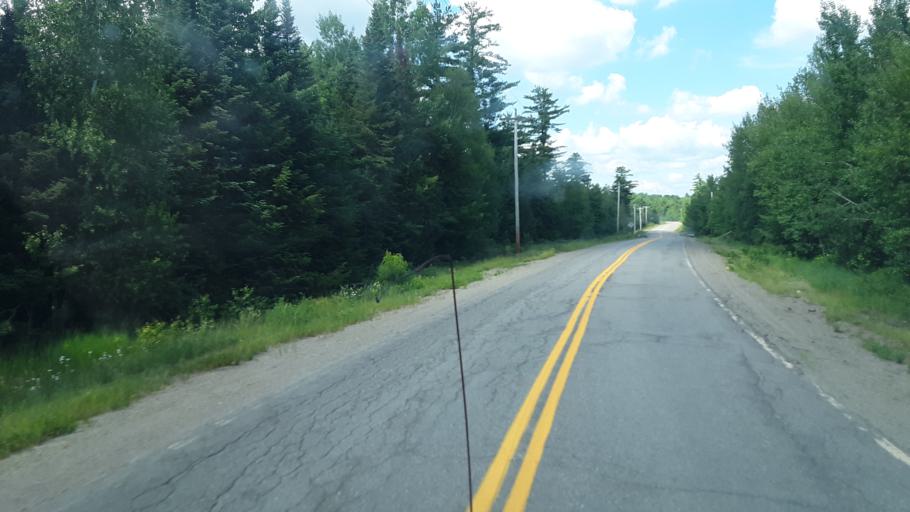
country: US
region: Maine
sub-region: Washington County
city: Calais
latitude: 45.1229
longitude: -67.4991
